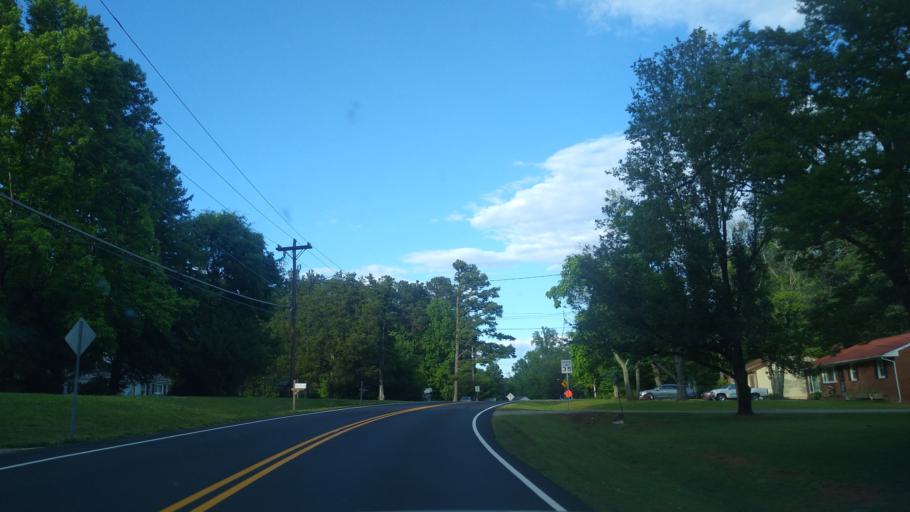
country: US
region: North Carolina
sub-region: Guilford County
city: McLeansville
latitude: 36.1604
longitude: -79.7355
